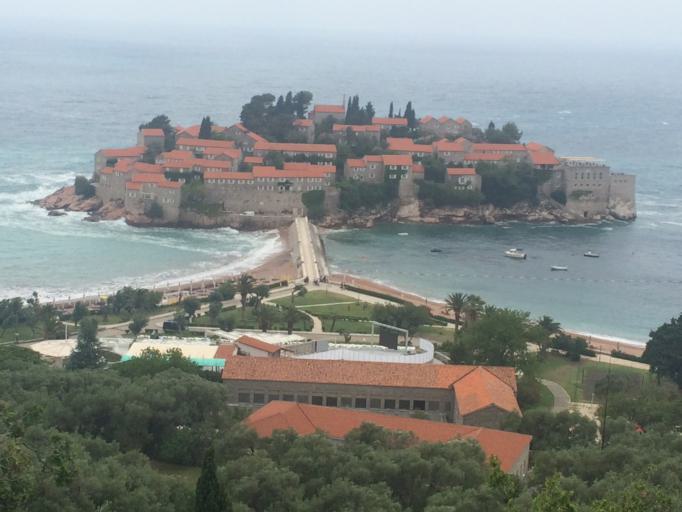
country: ME
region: Budva
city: Budva
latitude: 42.2581
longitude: 18.8960
